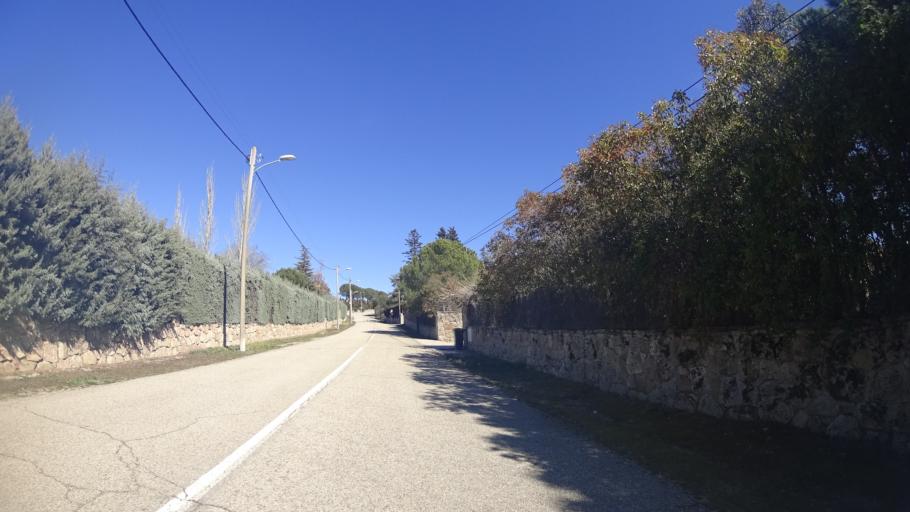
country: ES
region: Madrid
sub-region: Provincia de Madrid
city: Colmenarejo
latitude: 40.5513
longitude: -3.9893
